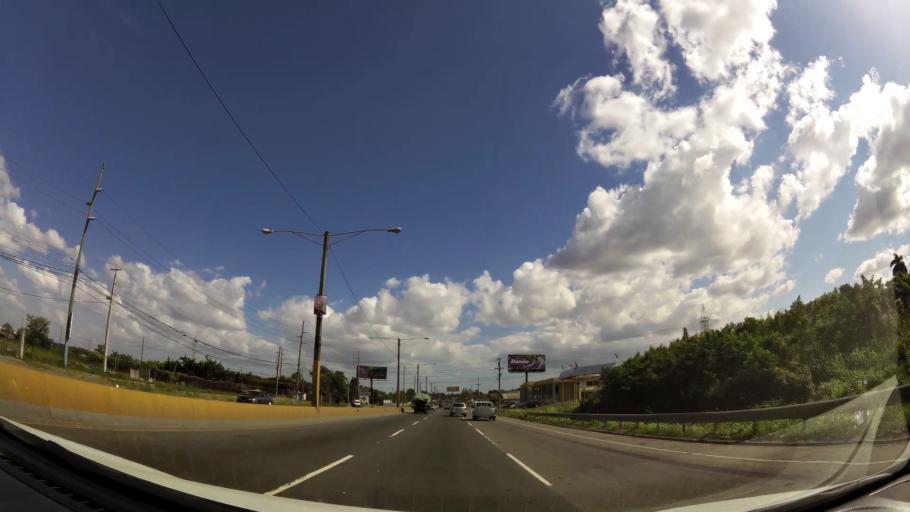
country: DO
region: Santo Domingo
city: Santo Domingo Oeste
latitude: 18.5553
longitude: -70.0567
